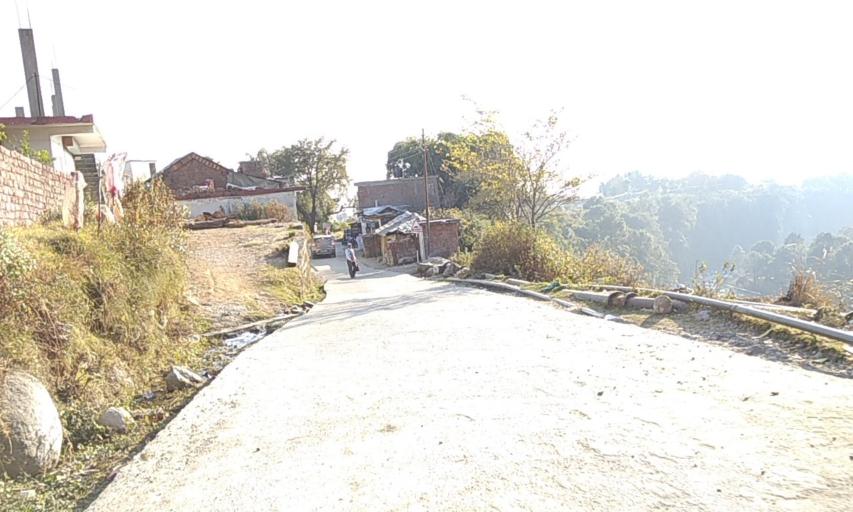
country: IN
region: Himachal Pradesh
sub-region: Kangra
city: Palampur
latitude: 32.1306
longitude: 76.5360
